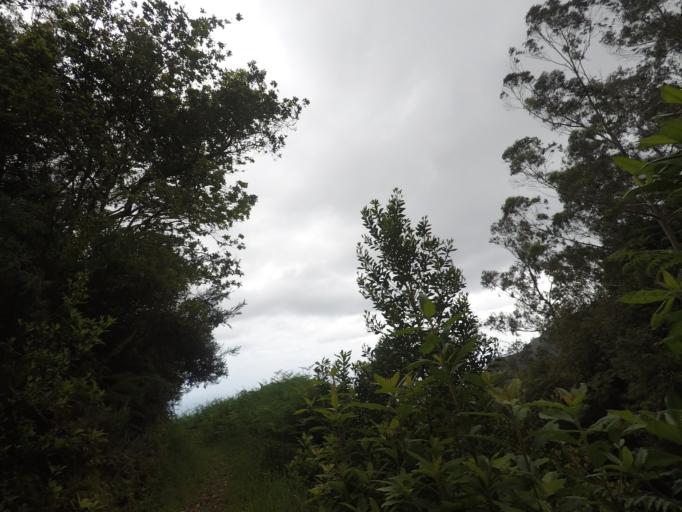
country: PT
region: Madeira
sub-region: Santa Cruz
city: Santa Cruz
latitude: 32.7488
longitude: -16.8244
